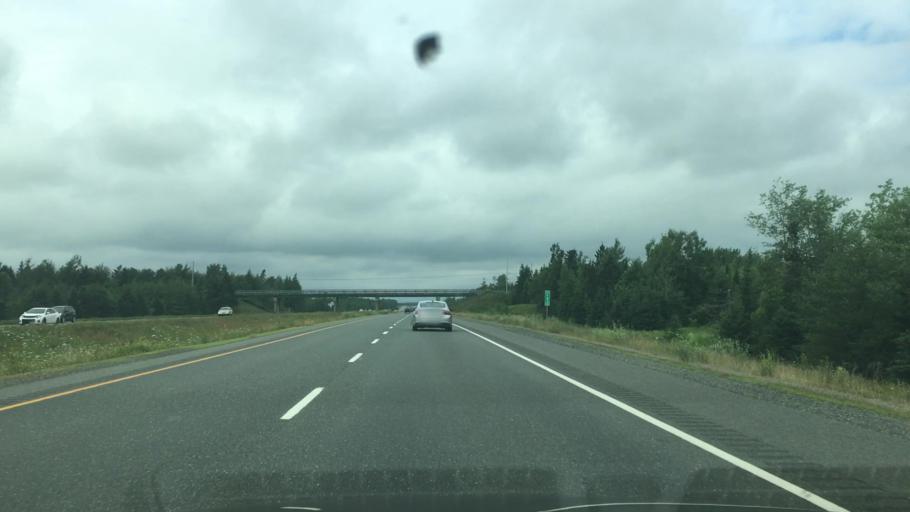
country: CA
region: Nova Scotia
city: Truro
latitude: 45.3825
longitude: -63.3636
